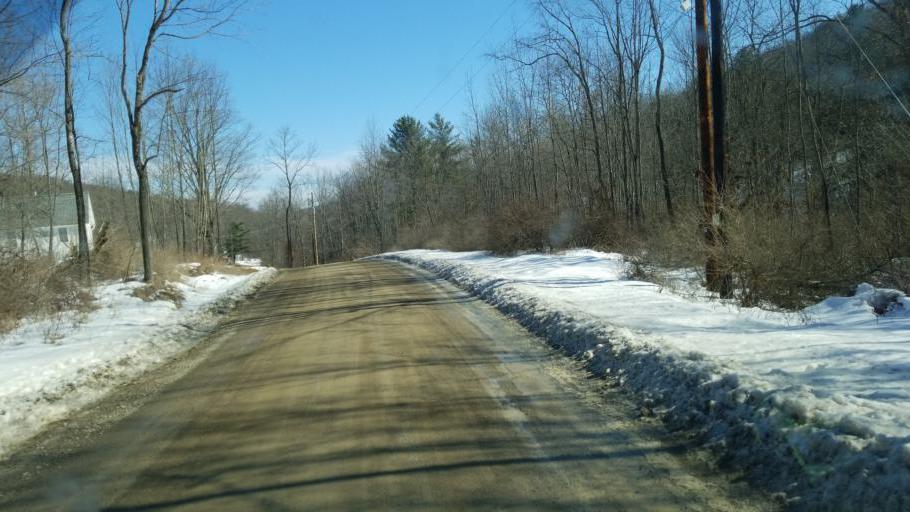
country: US
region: New York
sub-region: Allegany County
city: Alfred
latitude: 42.2475
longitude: -77.7133
